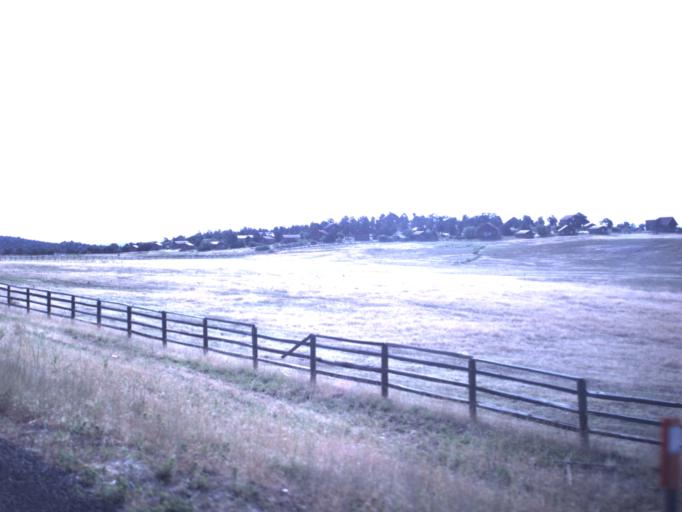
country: US
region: Utah
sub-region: Washington County
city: Hildale
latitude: 37.2454
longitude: -112.8068
